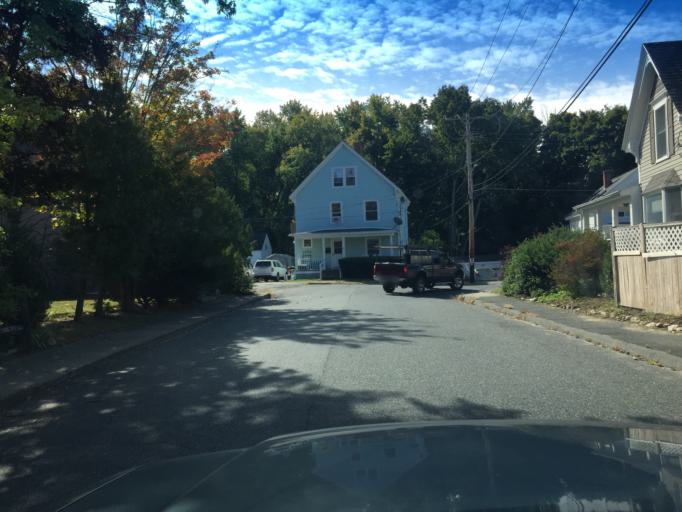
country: US
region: Massachusetts
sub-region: Middlesex County
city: Hudson
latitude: 42.3889
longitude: -71.5610
